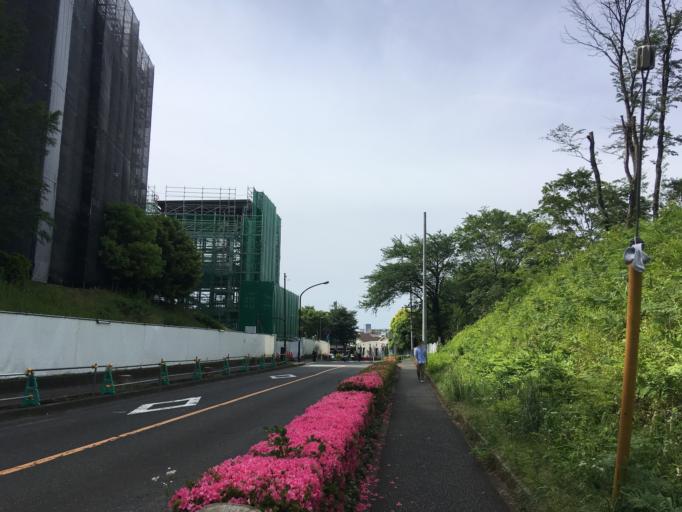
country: JP
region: Kanagawa
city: Minami-rinkan
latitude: 35.5100
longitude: 139.4695
